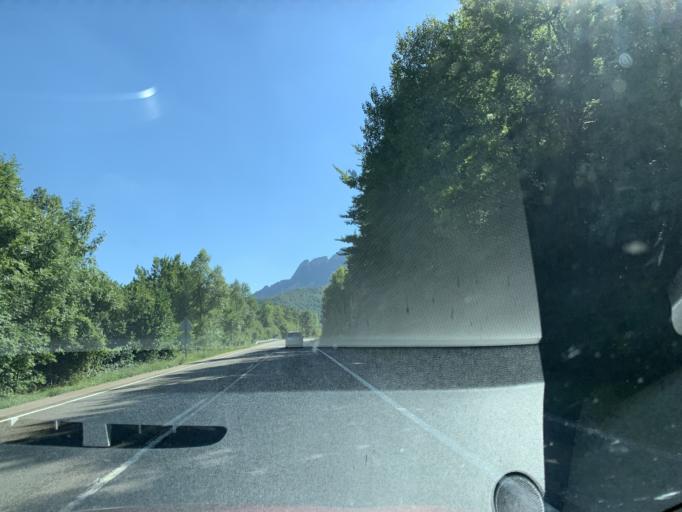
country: ES
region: Aragon
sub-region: Provincia de Huesca
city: Hoz de Jaca
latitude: 42.7091
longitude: -0.3112
